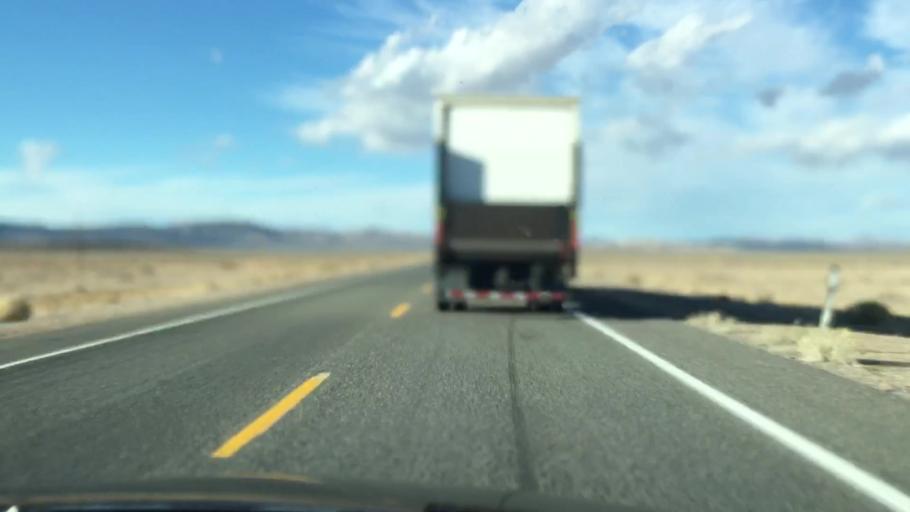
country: US
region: Nevada
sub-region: Esmeralda County
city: Goldfield
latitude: 37.4330
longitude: -117.1615
